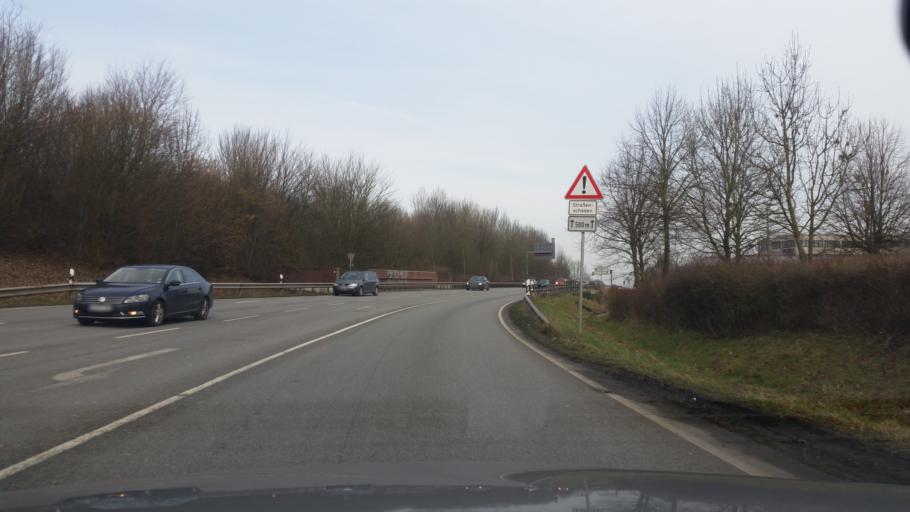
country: DE
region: North Rhine-Westphalia
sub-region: Regierungsbezirk Detmold
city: Oerlinghausen
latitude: 51.9983
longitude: 8.6072
